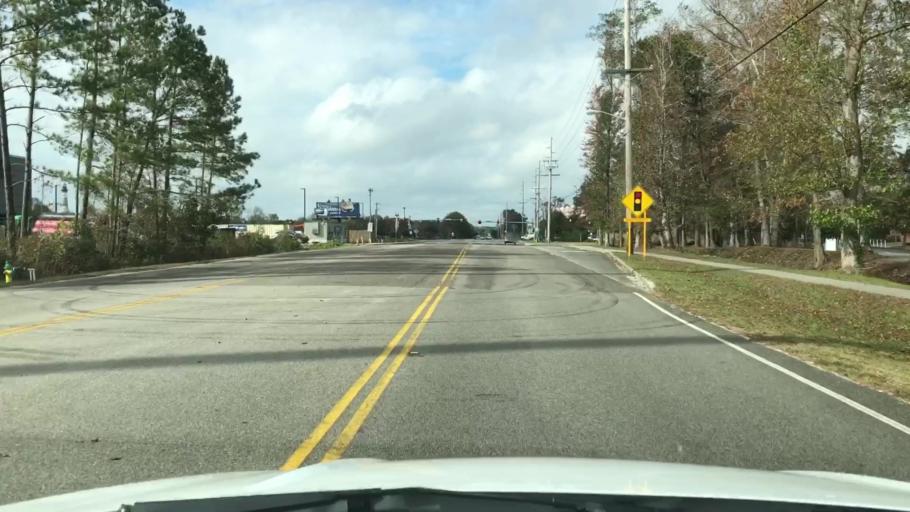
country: US
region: South Carolina
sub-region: Horry County
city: Myrtle Beach
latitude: 33.7142
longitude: -78.8708
